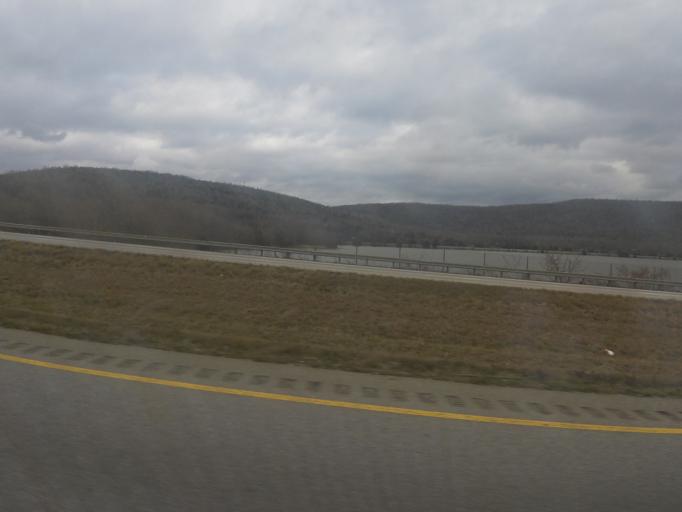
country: US
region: Tennessee
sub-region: Marion County
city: Jasper
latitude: 35.0296
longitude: -85.5733
